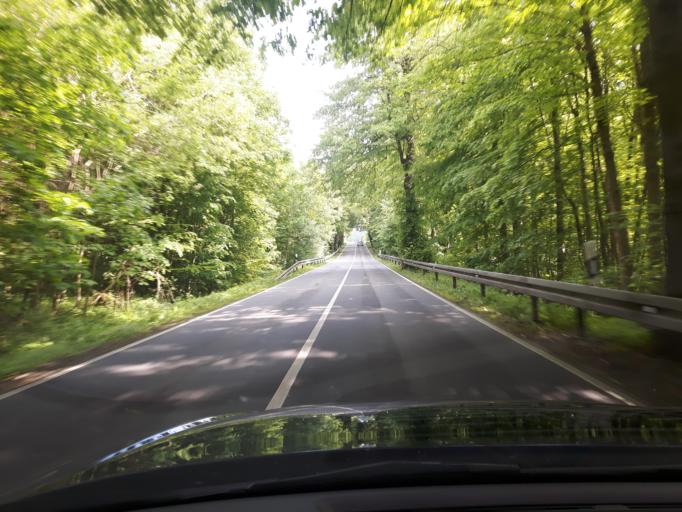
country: DE
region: Mecklenburg-Vorpommern
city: Gross Wokern
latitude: 53.6329
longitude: 12.4749
